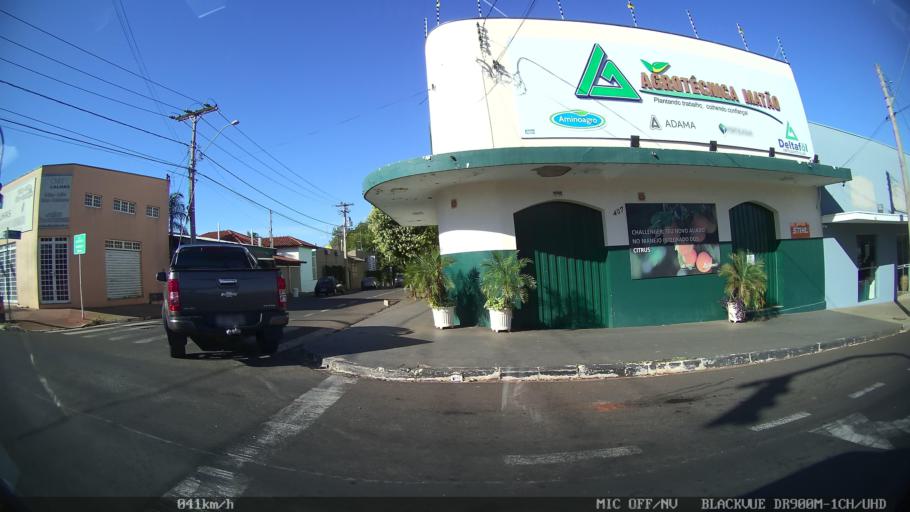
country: BR
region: Sao Paulo
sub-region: Olimpia
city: Olimpia
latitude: -20.7367
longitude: -48.9037
